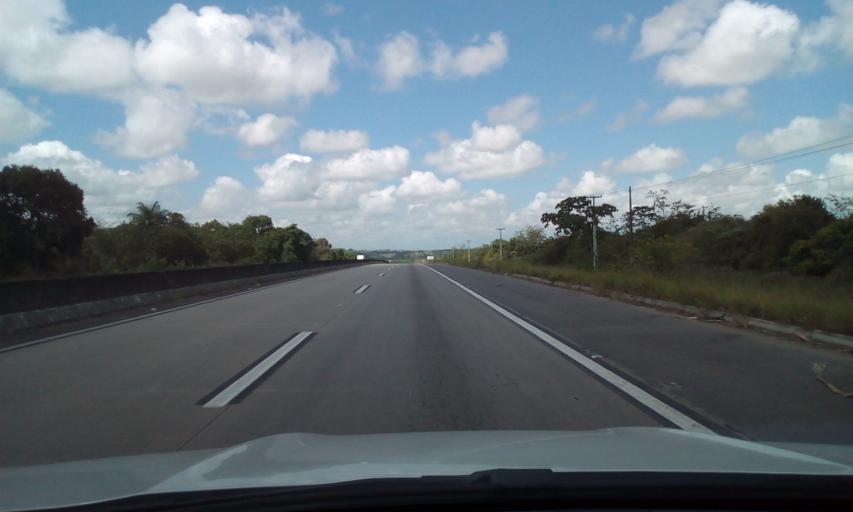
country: BR
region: Paraiba
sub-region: Alhandra
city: Alhandra
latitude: -7.4214
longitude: -34.9620
